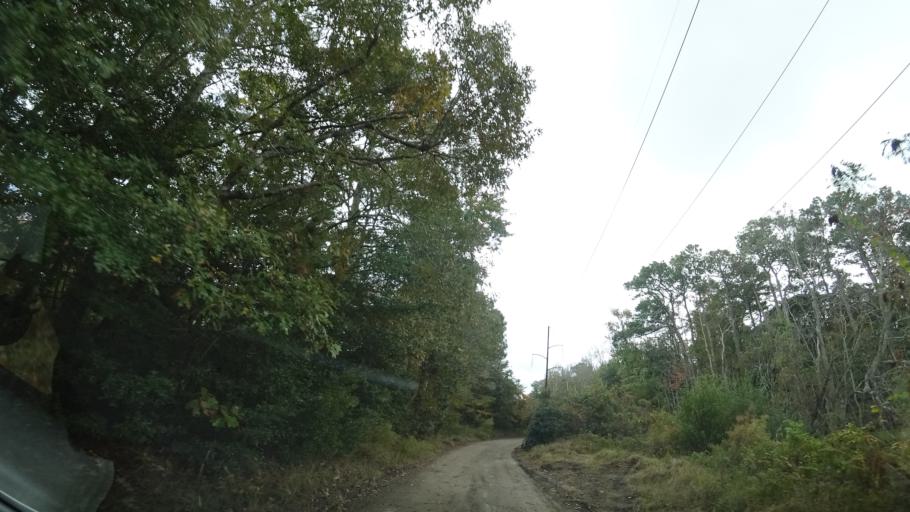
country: US
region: North Carolina
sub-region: Dare County
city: Kill Devil Hills
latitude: 35.9937
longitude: -75.6661
